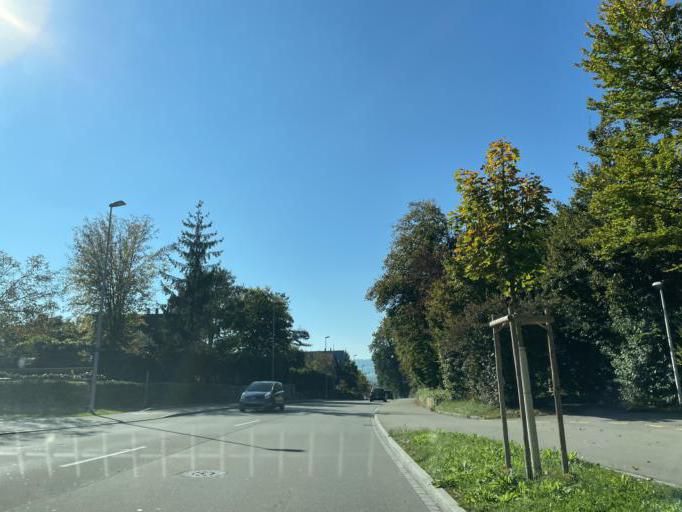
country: CH
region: Zurich
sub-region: Bezirk Uster
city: Uster / Ober-Uster
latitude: 47.3559
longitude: 8.7263
